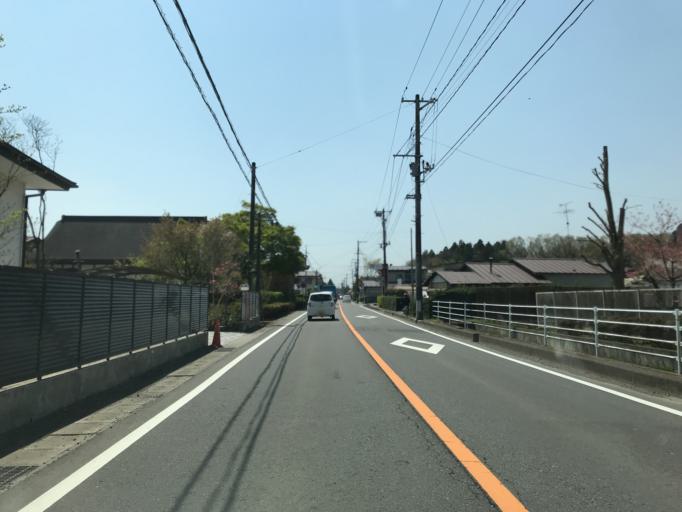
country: JP
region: Fukushima
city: Ishikawa
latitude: 37.1533
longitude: 140.3504
